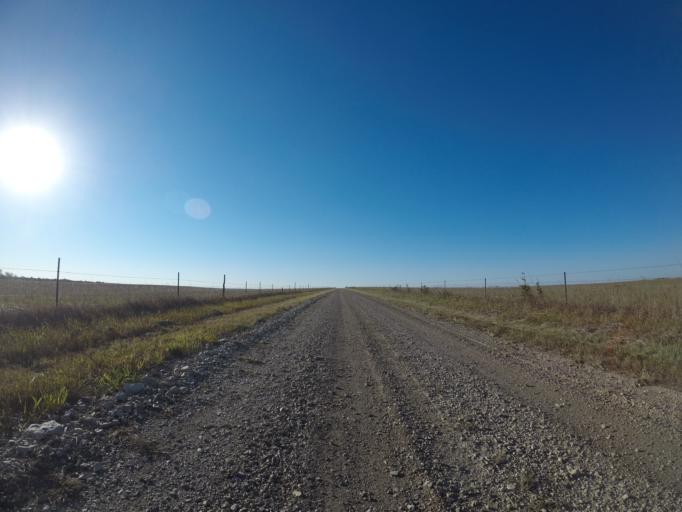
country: US
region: Kansas
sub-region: Wabaunsee County
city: Alma
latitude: 38.9393
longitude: -96.4641
